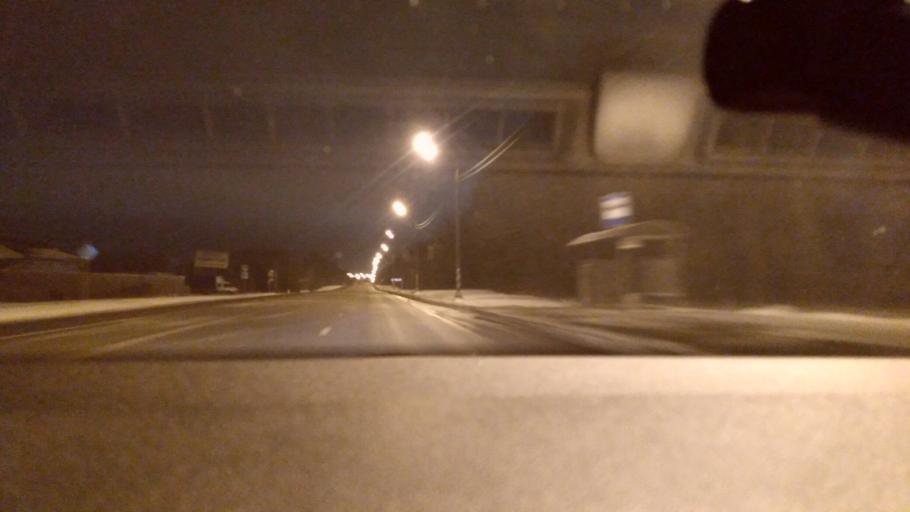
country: RU
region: Moskovskaya
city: Bronnitsy
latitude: 55.4781
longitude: 38.1820
